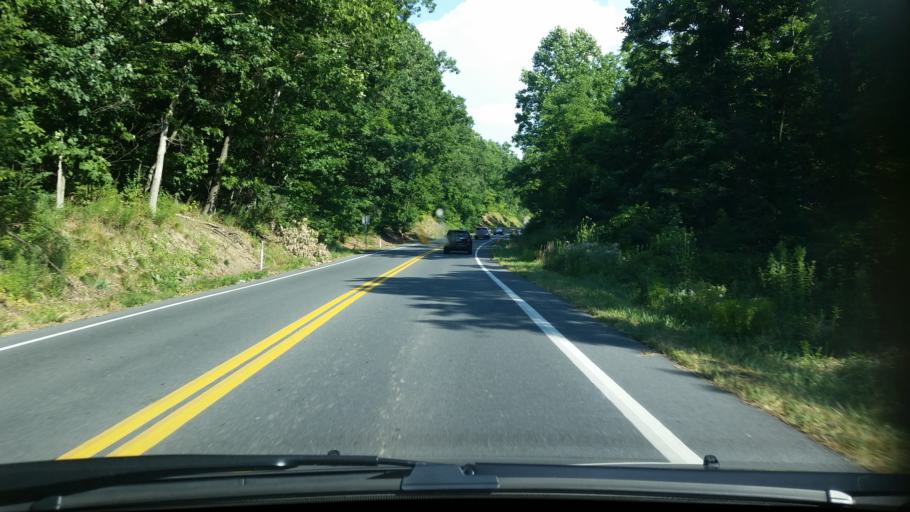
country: US
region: Pennsylvania
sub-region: Dauphin County
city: Rutherford
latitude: 40.2937
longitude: -76.7667
